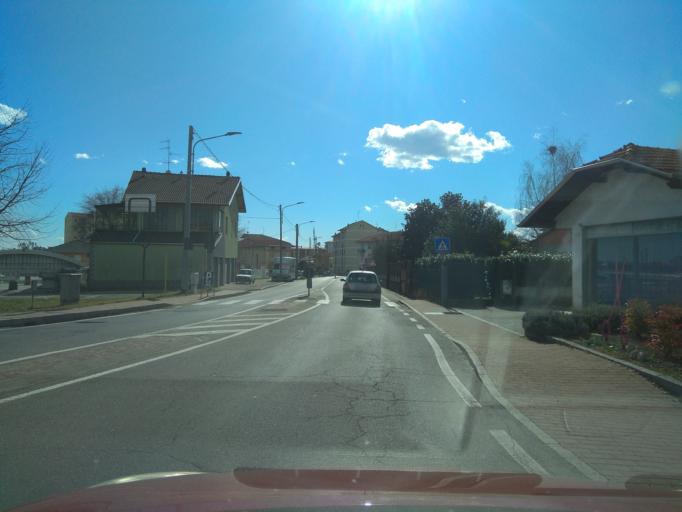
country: IT
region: Piedmont
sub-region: Provincia di Biella
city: Cossato
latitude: 45.5765
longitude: 8.1810
